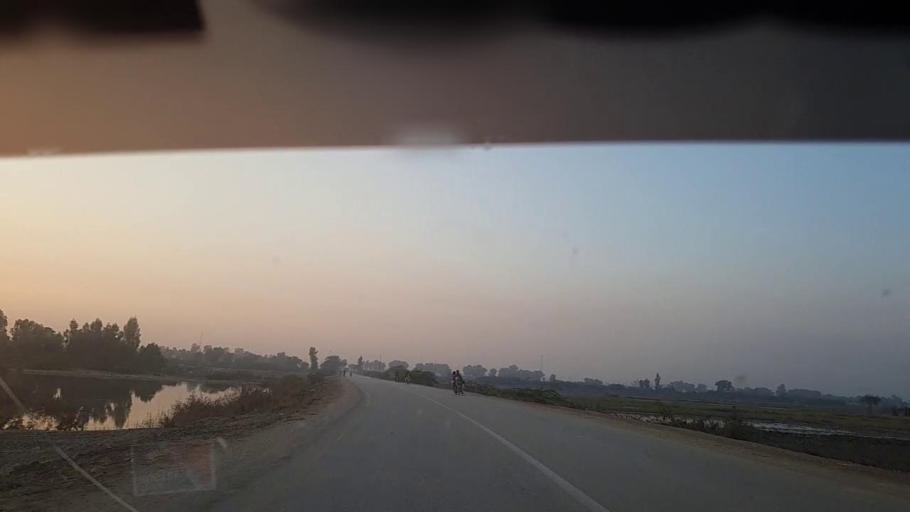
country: PK
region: Sindh
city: Ranipur
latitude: 27.2708
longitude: 68.5171
